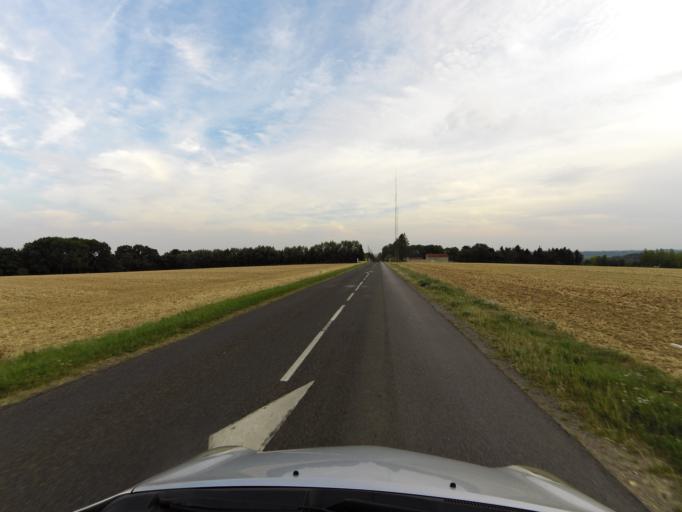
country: FR
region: Picardie
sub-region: Departement de l'Aisne
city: Bruyeres-et-Montberault
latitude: 49.4924
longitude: 3.6691
